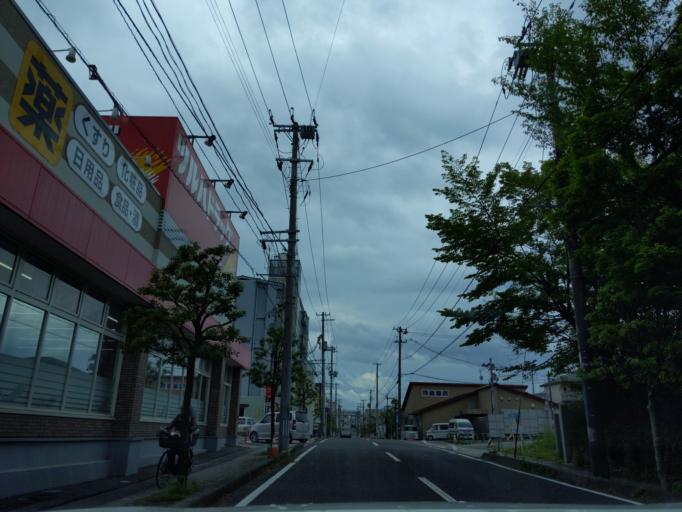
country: JP
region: Fukushima
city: Koriyama
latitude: 37.3910
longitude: 140.3720
